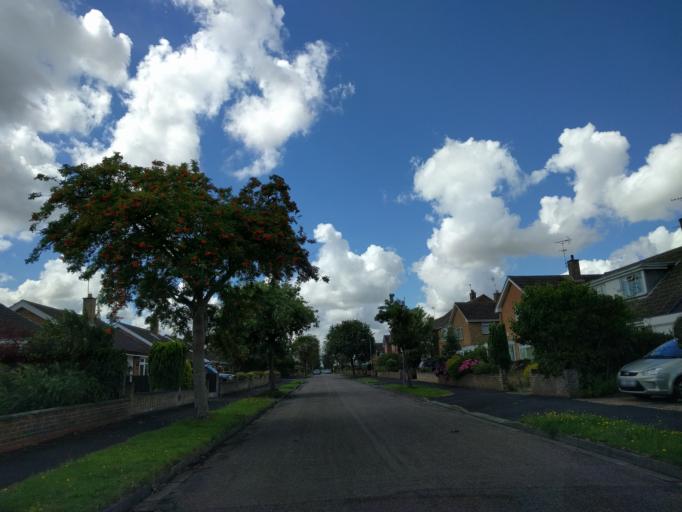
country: GB
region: England
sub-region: Nottinghamshire
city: Newark on Trent
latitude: 53.0666
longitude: -0.8210
